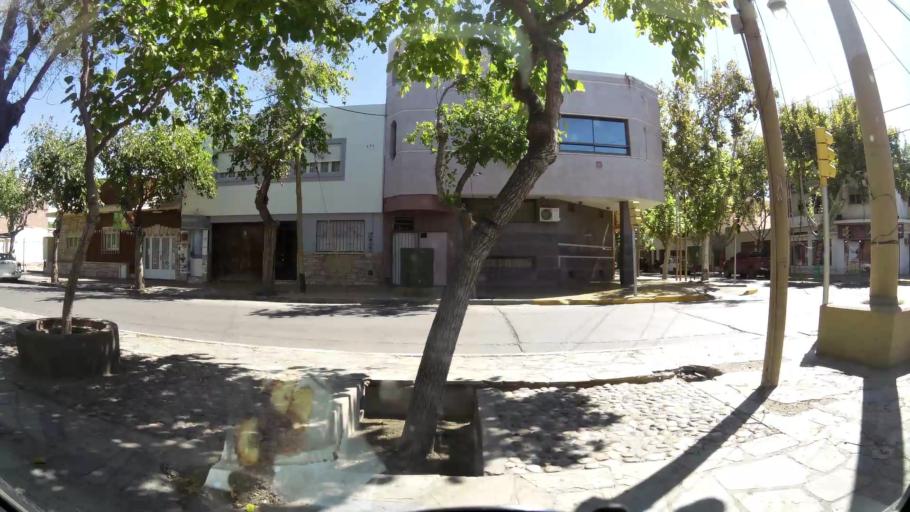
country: AR
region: San Juan
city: San Juan
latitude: -31.5328
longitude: -68.5218
